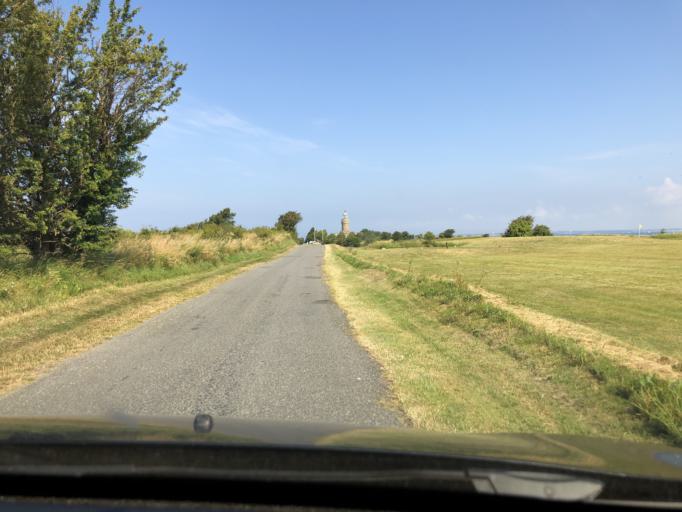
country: DK
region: South Denmark
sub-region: Faaborg-Midtfyn Kommune
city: Faaborg
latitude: 54.9664
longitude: 10.2103
